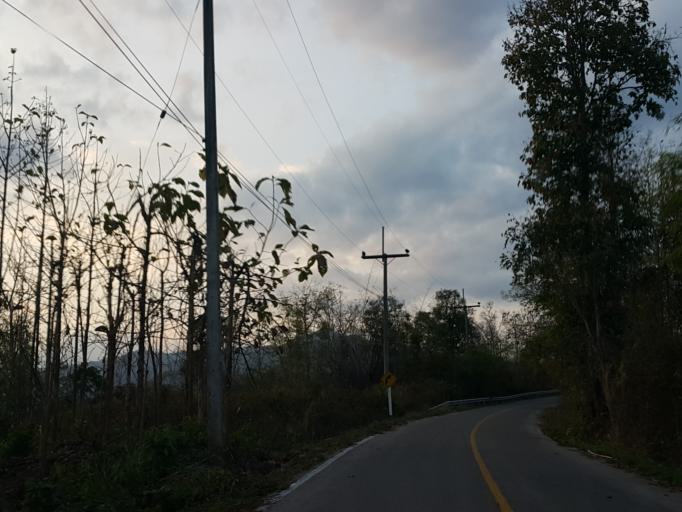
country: TH
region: Lampang
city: Mueang Pan
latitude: 18.8024
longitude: 99.4842
